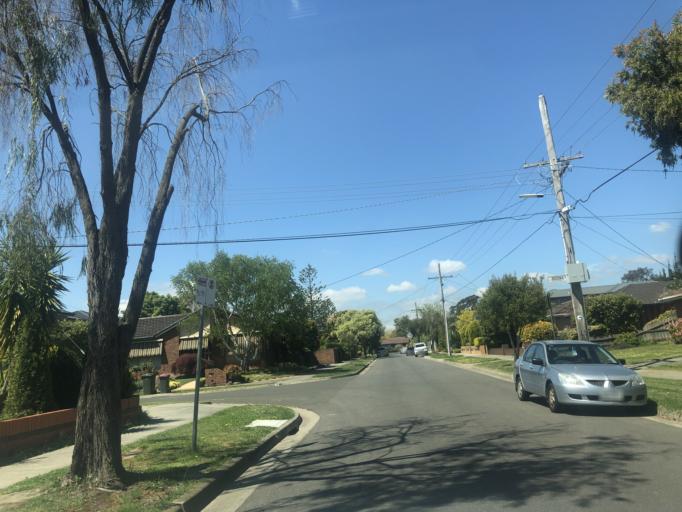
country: AU
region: Victoria
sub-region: Monash
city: Notting Hill
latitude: -37.9009
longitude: 145.1643
